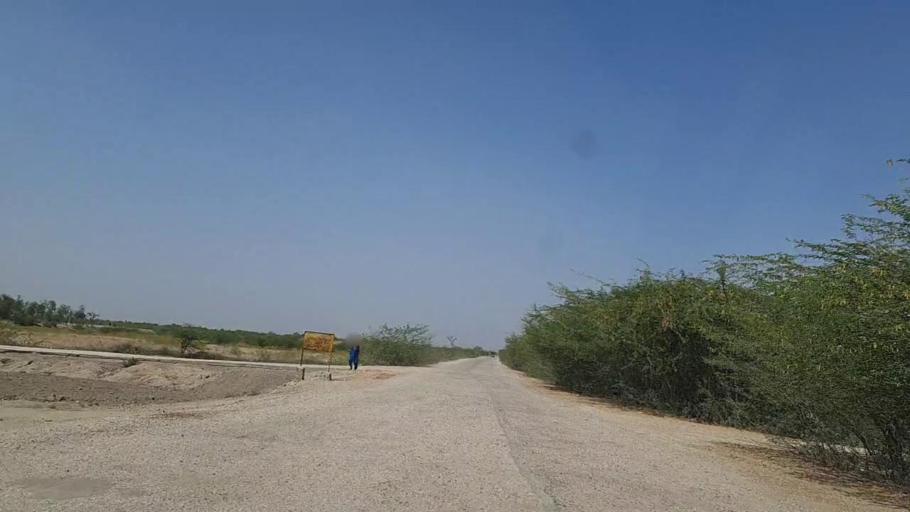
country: PK
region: Sindh
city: Naukot
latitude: 24.6386
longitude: 69.2880
